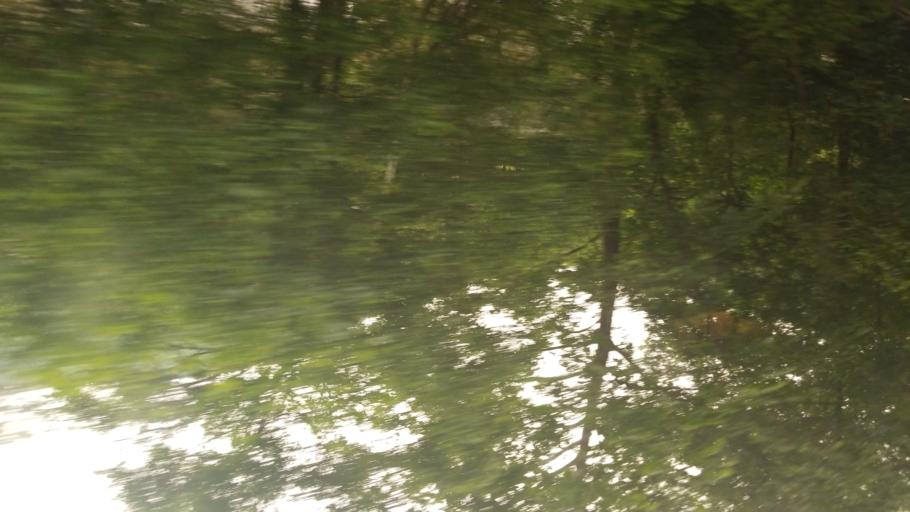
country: US
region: Pennsylvania
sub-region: Fayette County
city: South Connellsville
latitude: 39.9677
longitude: -79.5154
